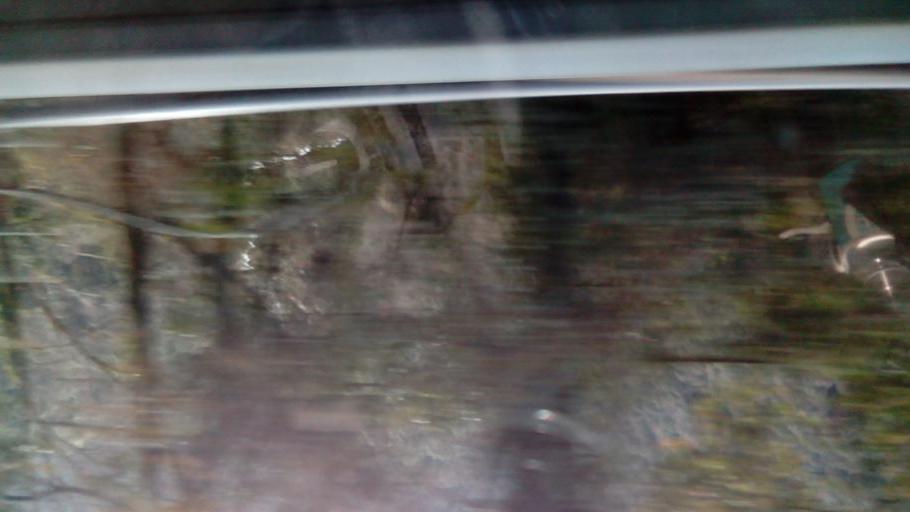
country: TW
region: Taiwan
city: Daxi
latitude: 24.4108
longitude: 121.3602
